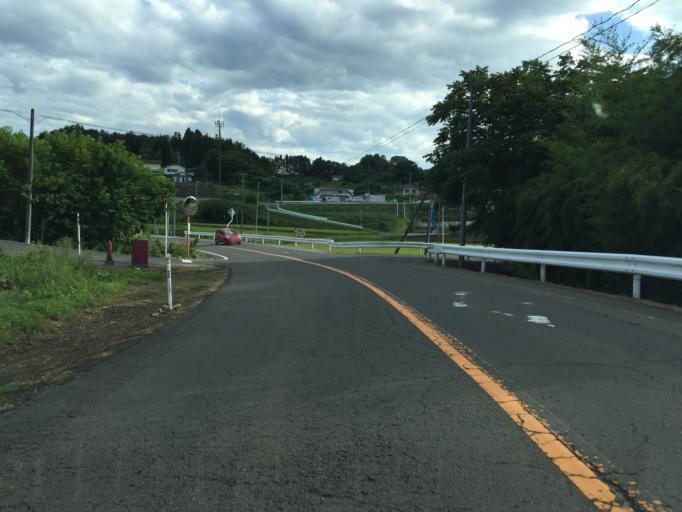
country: JP
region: Fukushima
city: Fukushima-shi
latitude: 37.6710
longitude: 140.5258
